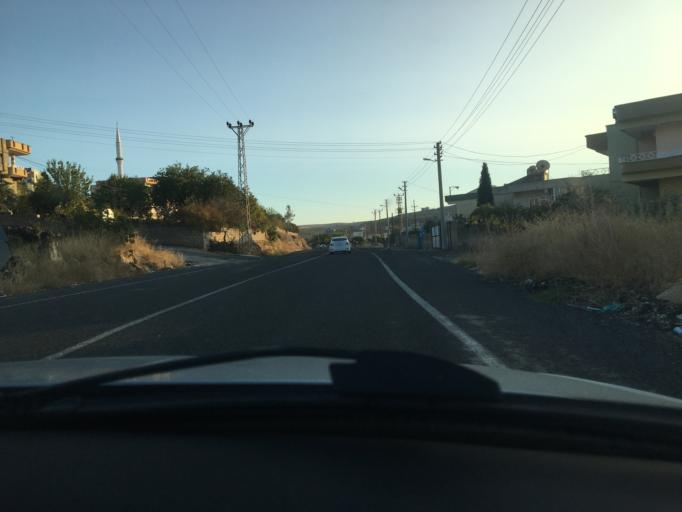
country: TR
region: Sanliurfa
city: Halfeti
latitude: 37.2127
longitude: 37.9634
